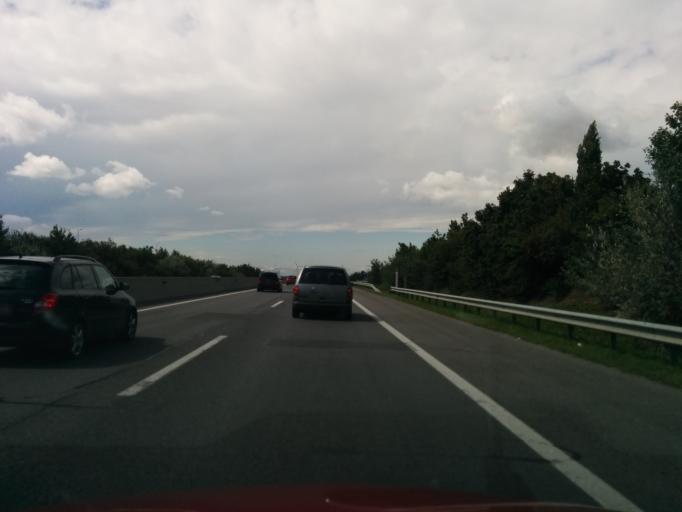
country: AT
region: Burgenland
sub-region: Politischer Bezirk Neusiedl am See
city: Zurndorf
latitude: 47.9411
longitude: 16.9586
